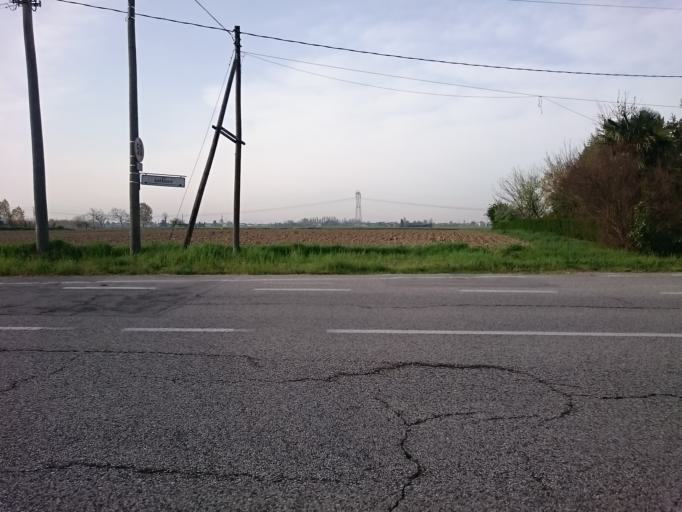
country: IT
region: Veneto
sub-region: Provincia di Padova
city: Albignasego
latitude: 45.3643
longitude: 11.8826
